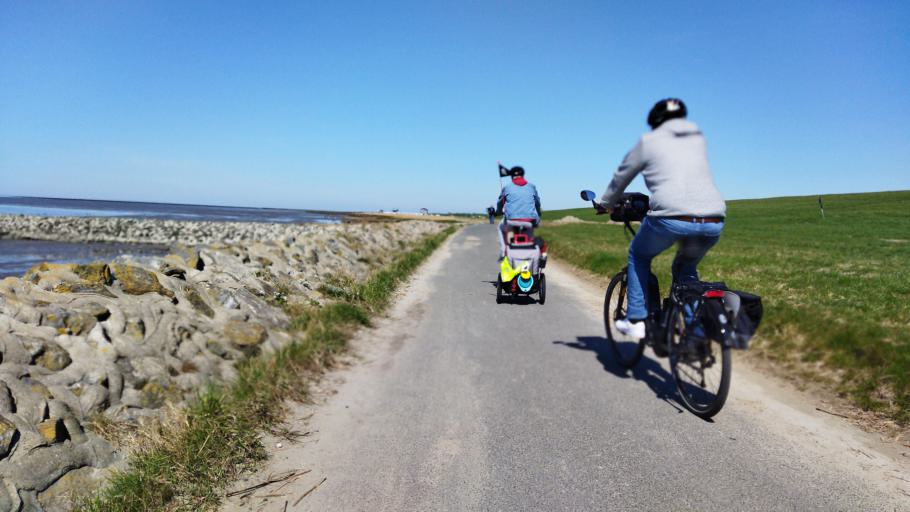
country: DE
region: Lower Saxony
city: Wremen
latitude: 53.6290
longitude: 8.5043
